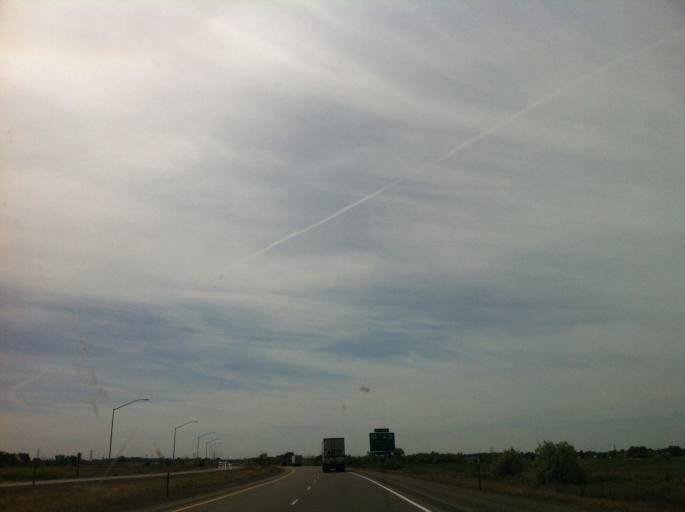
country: US
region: Oregon
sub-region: Malheur County
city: Ontario
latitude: 44.0644
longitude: -116.9947
